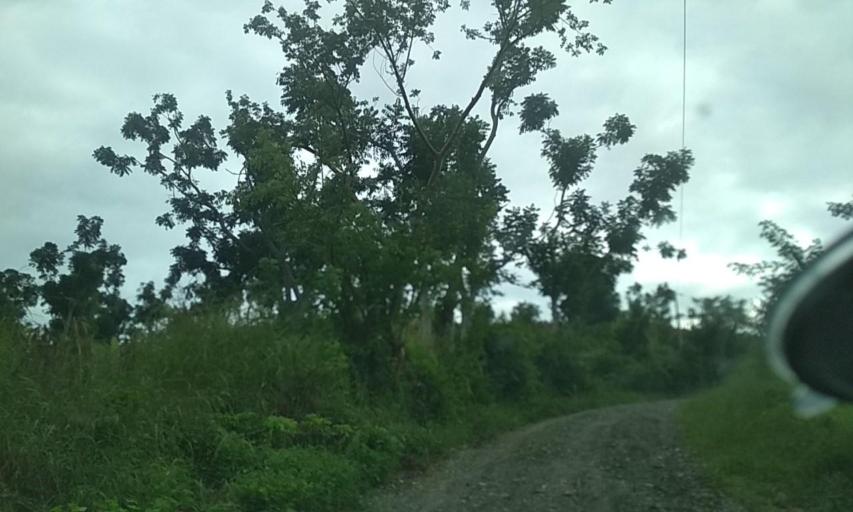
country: MX
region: Veracruz
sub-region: Papantla
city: Polutla
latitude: 20.5846
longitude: -97.2767
